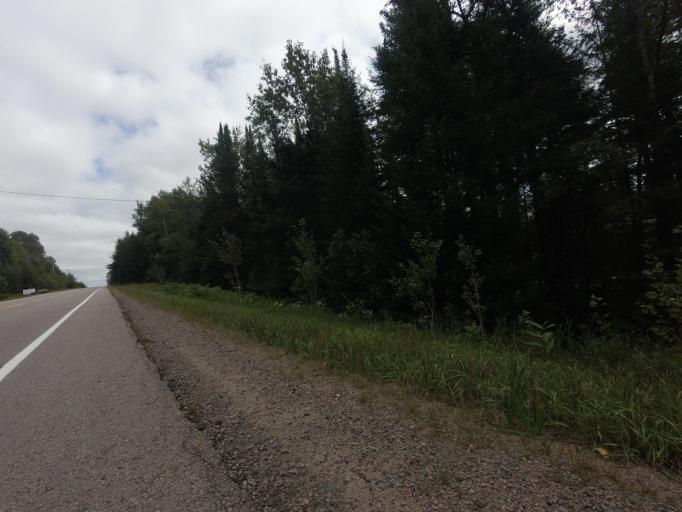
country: CA
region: Ontario
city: Omemee
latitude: 44.8981
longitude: -78.4540
